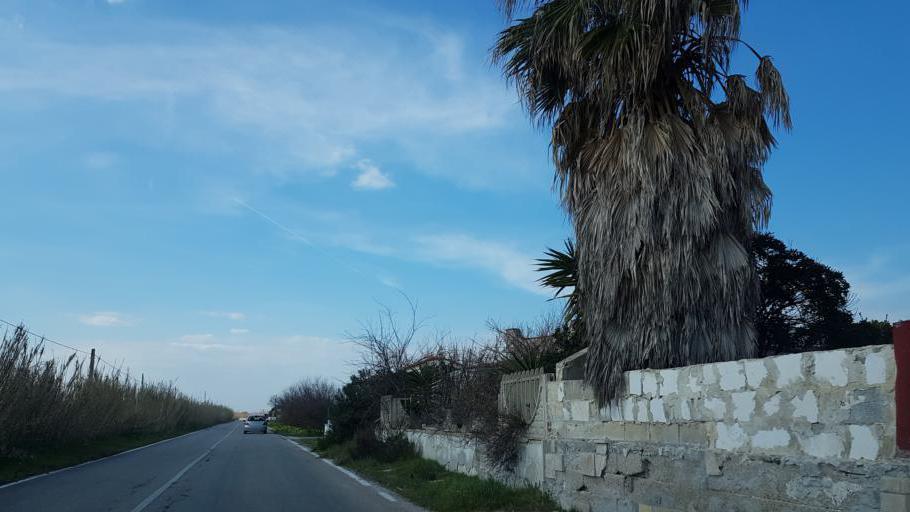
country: IT
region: Apulia
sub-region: Provincia di Brindisi
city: Brindisi
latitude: 40.6829
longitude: 17.8856
